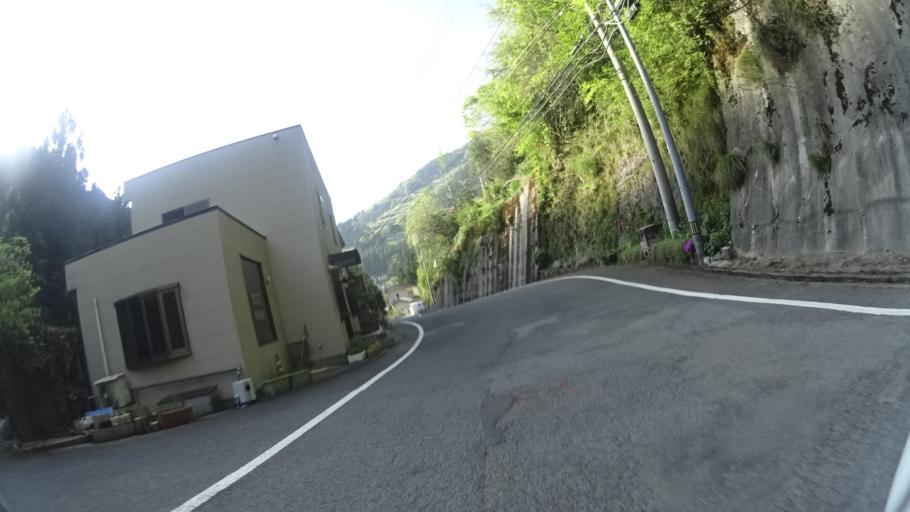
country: JP
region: Tokushima
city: Ikedacho
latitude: 33.8770
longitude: 133.9386
